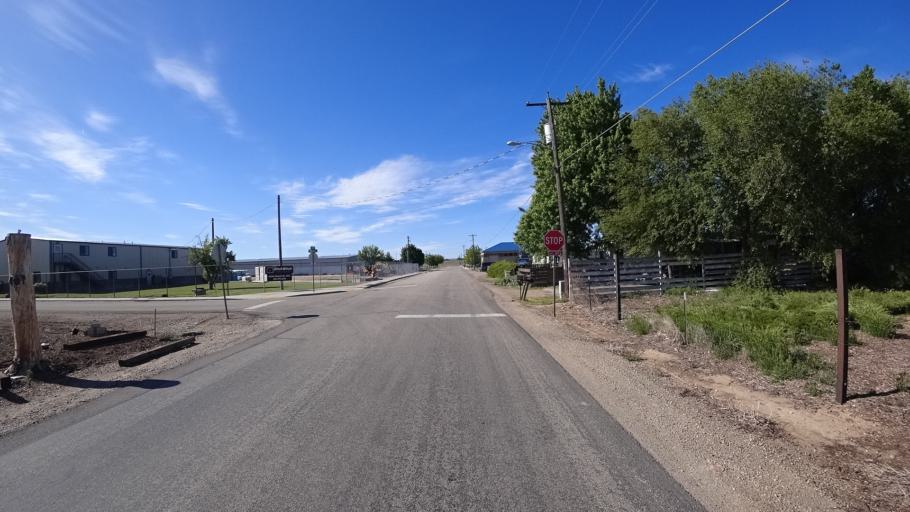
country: US
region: Idaho
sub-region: Ada County
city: Garden City
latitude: 43.5793
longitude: -116.2611
